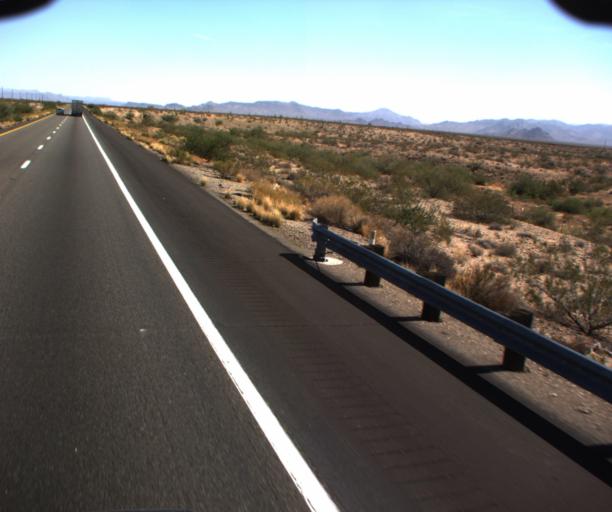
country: US
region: Arizona
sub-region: Mohave County
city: Kingman
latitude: 34.9822
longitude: -114.1397
